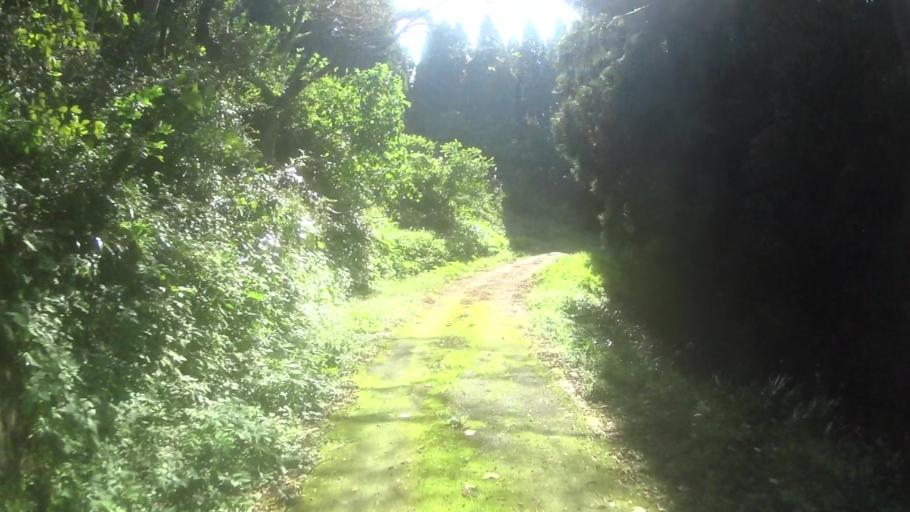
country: JP
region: Kyoto
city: Miyazu
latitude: 35.7130
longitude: 135.1633
